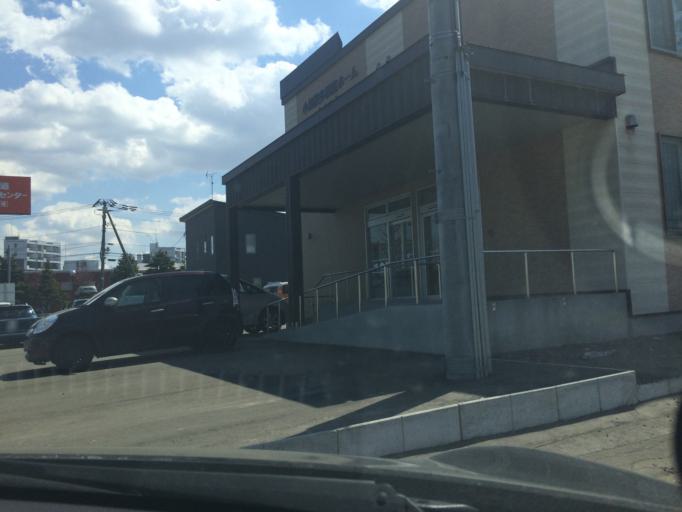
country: JP
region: Hokkaido
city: Sapporo
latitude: 43.0507
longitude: 141.3777
